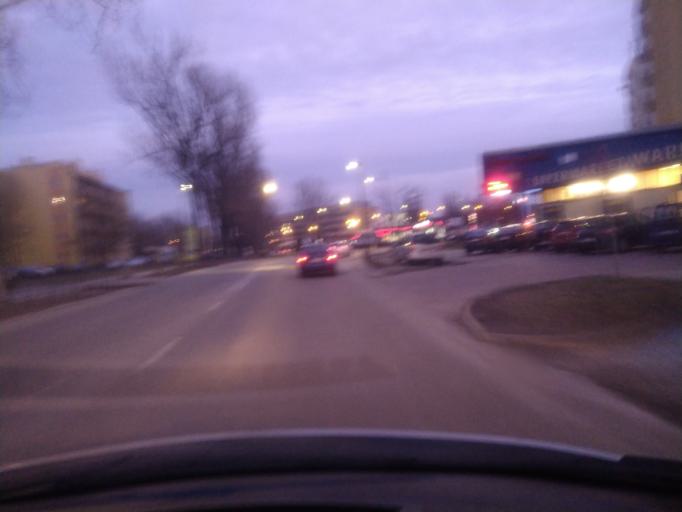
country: PL
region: Masovian Voivodeship
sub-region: Warszawa
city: Praga Poludnie
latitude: 52.2379
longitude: 21.0861
